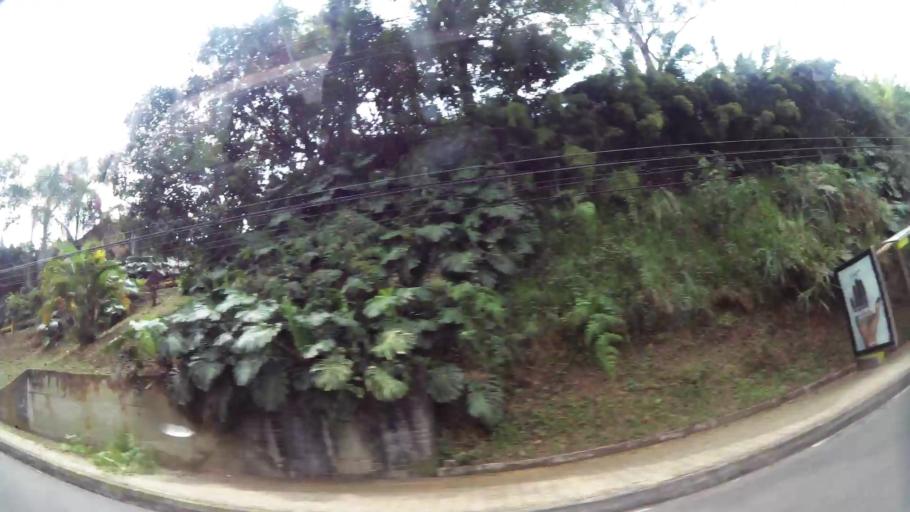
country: CO
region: Antioquia
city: Envigado
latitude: 6.1947
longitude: -75.5734
